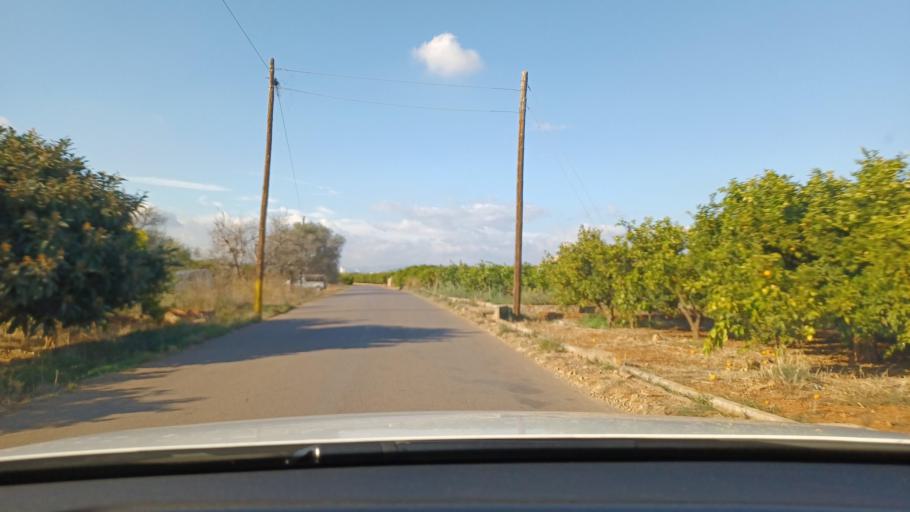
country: ES
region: Valencia
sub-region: Provincia de Castello
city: Betxi
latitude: 39.9399
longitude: -0.2107
